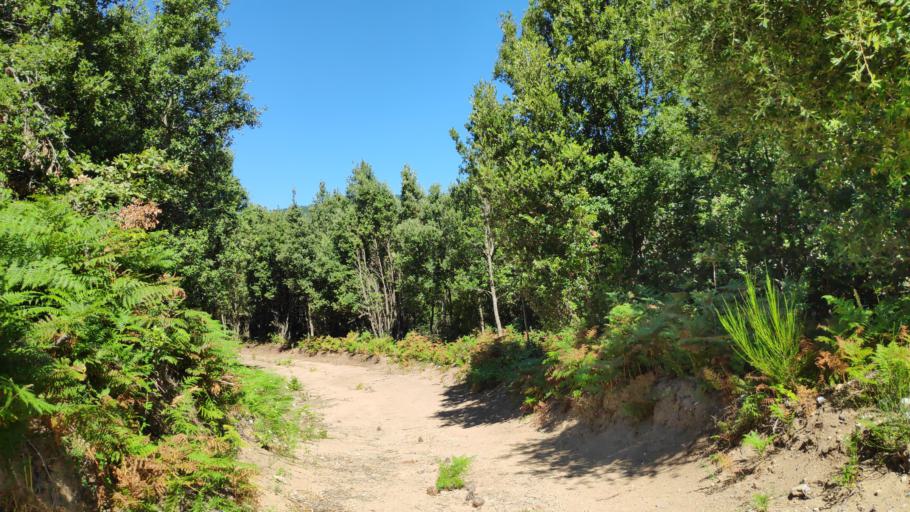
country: IT
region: Calabria
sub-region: Provincia di Vibo-Valentia
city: Nardodipace
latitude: 38.4786
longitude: 16.3918
